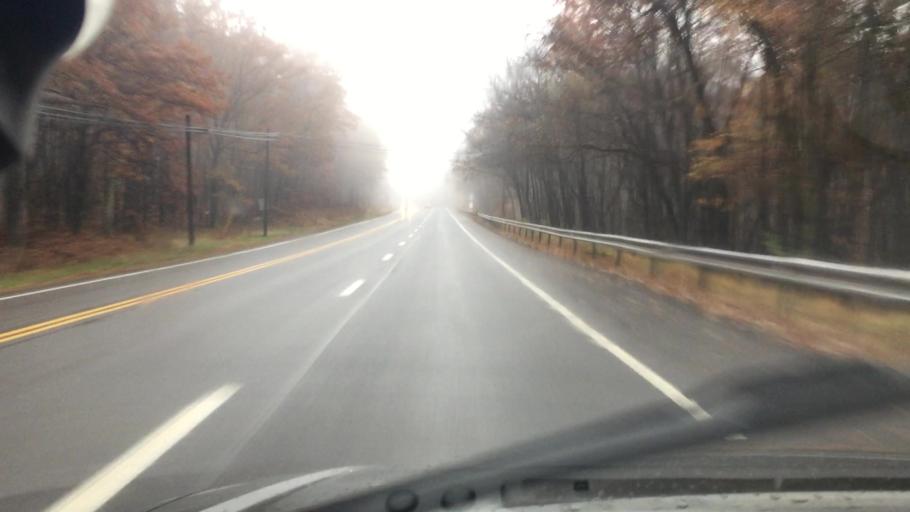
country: US
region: Pennsylvania
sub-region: Luzerne County
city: Freeland
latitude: 41.0696
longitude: -75.9598
